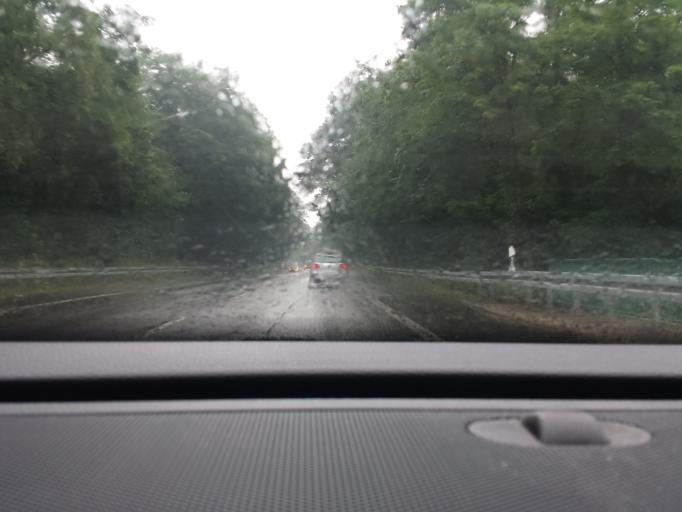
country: DE
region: North Rhine-Westphalia
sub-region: Regierungsbezirk Munster
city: Gronau
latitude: 52.2092
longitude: 7.0225
